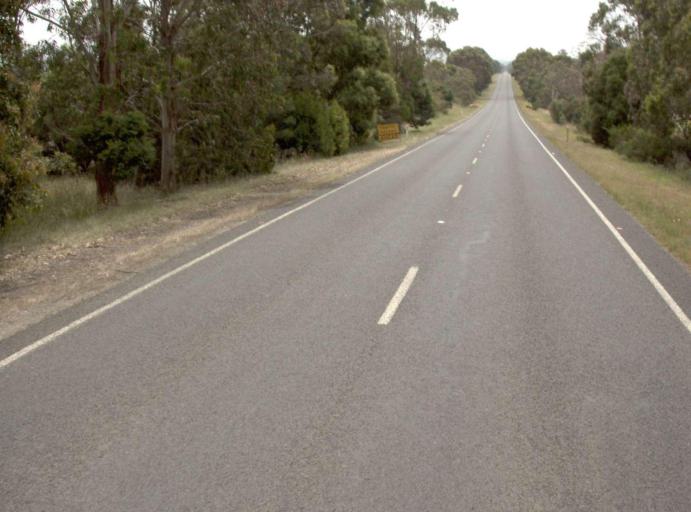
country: AU
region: Victoria
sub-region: Latrobe
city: Traralgon
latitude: -38.5039
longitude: 146.7105
